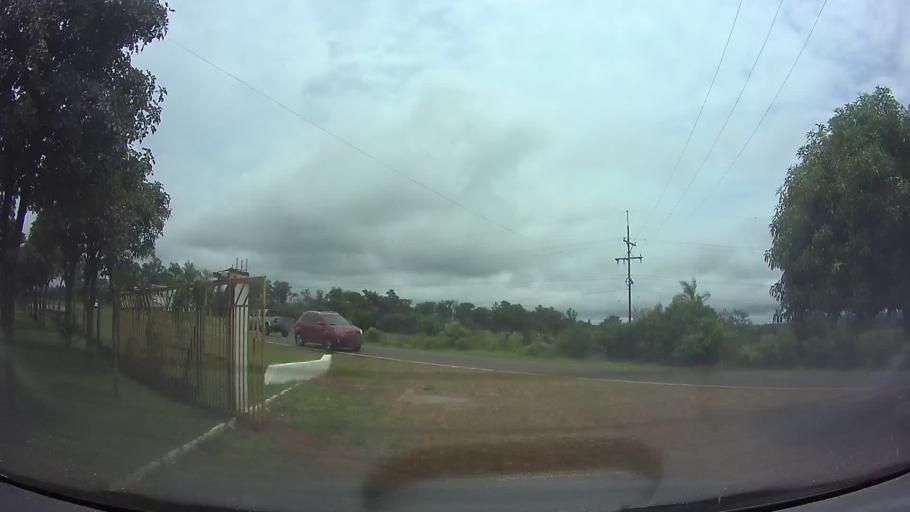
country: PY
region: Paraguari
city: Ybycui
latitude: -25.9963
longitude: -57.0507
